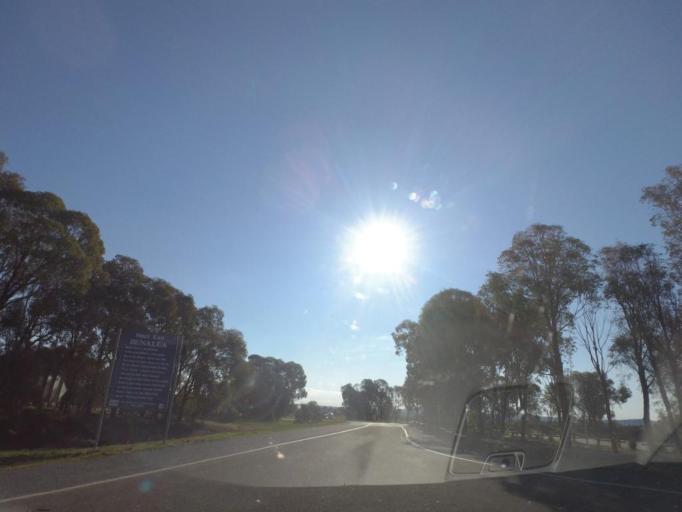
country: AU
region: Victoria
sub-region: Benalla
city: Benalla
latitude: -36.5013
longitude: 146.1027
